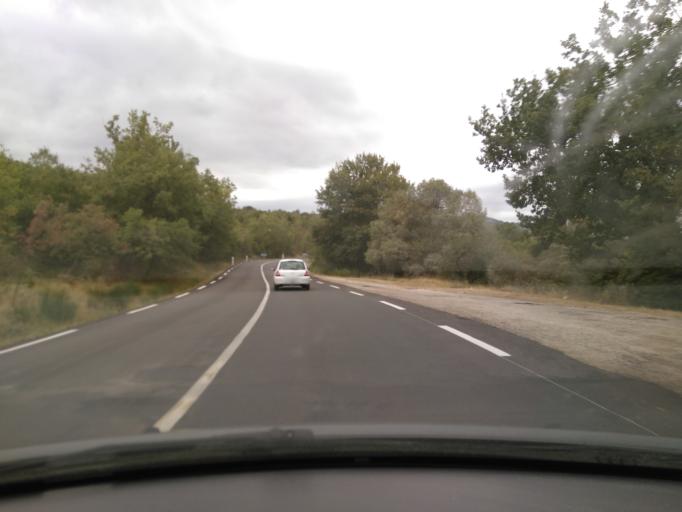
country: FR
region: Rhone-Alpes
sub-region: Departement de la Drome
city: Grignan
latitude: 44.4208
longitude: 4.8531
